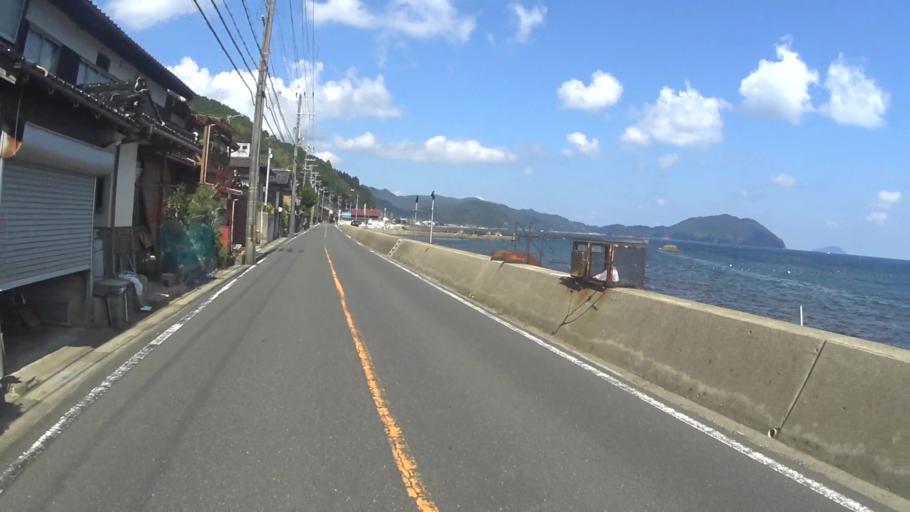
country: JP
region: Kyoto
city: Miyazu
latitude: 35.6475
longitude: 135.2520
